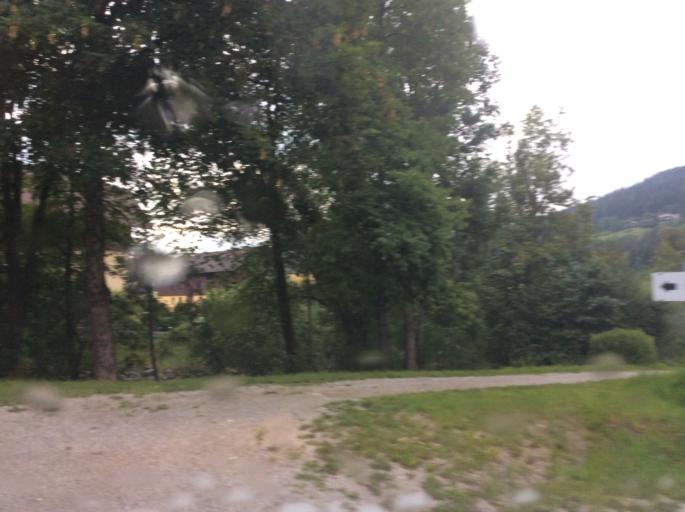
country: AT
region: Styria
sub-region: Politischer Bezirk Liezen
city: Schladming
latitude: 47.3976
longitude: 13.6963
